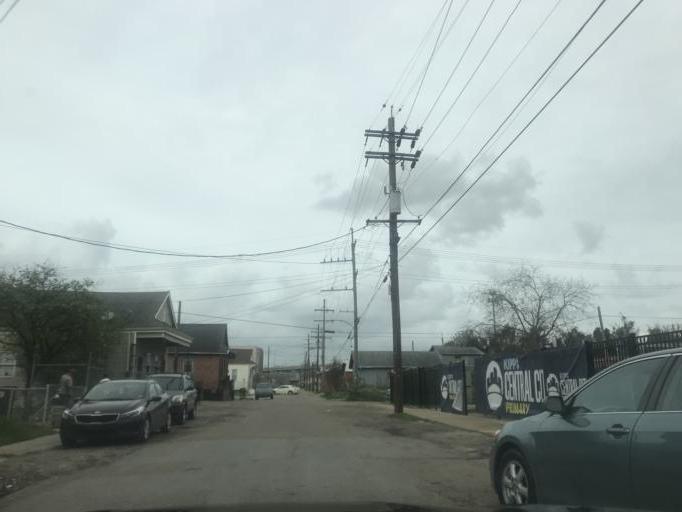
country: US
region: Louisiana
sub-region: Orleans Parish
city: New Orleans
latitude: 29.9478
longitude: -90.0901
